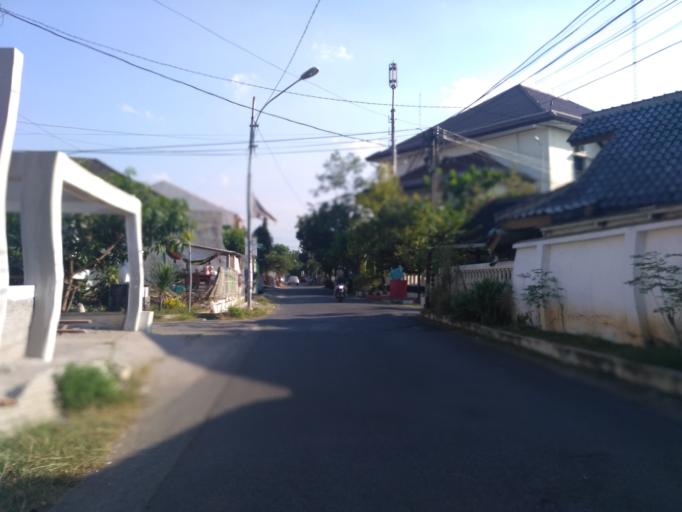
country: ID
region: Central Java
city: Semarang
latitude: -6.9985
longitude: 110.4505
